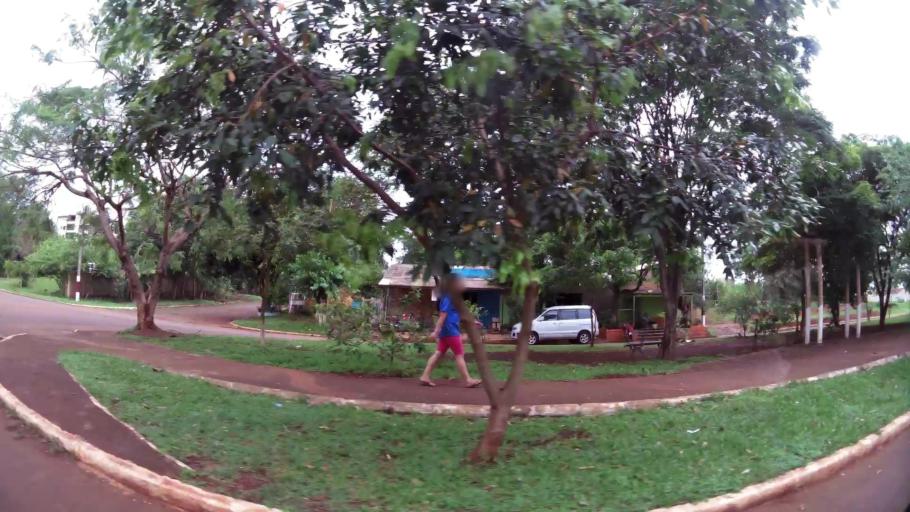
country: PY
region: Alto Parana
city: Ciudad del Este
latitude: -25.4052
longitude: -54.6350
